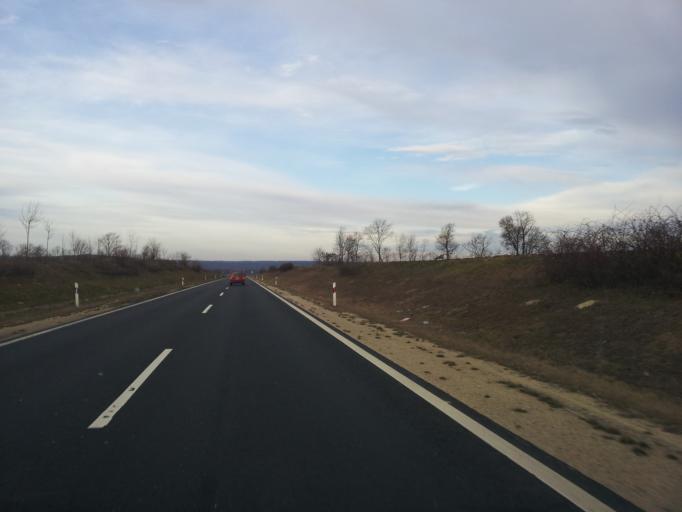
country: HU
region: Veszprem
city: Balatonkenese
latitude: 47.0629
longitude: 18.0981
